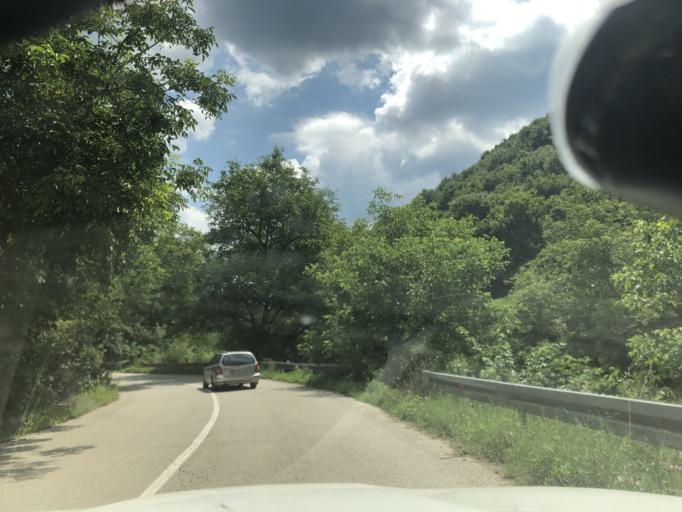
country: RS
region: Central Serbia
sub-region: Jablanicki Okrug
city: Medvega
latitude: 42.7883
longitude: 21.5833
